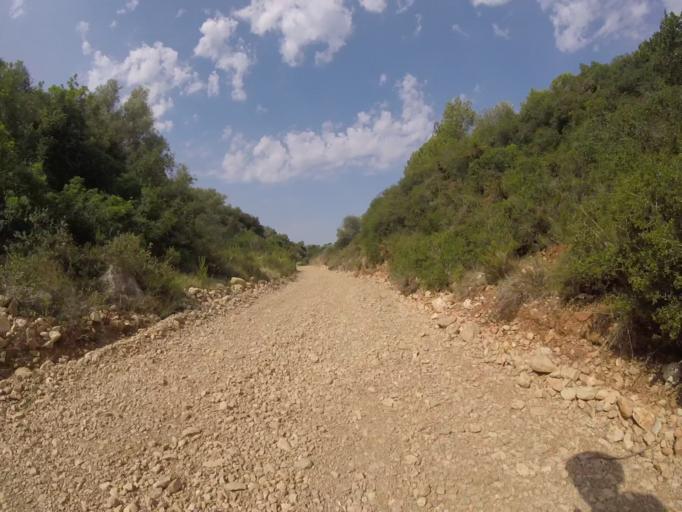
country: ES
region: Valencia
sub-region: Provincia de Castello
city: Alcala de Xivert
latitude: 40.3343
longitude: 0.1957
